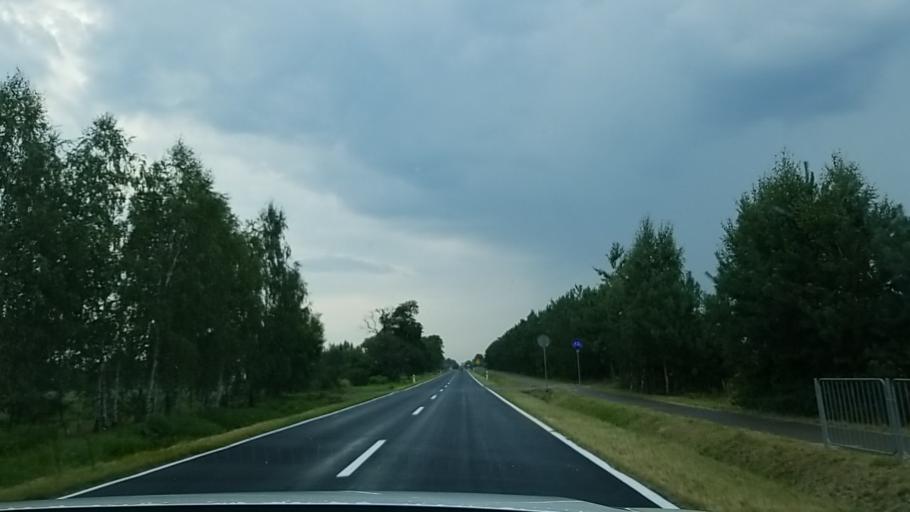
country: PL
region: Lublin Voivodeship
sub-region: Powiat wlodawski
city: Wlodawa
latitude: 51.5814
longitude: 23.5423
